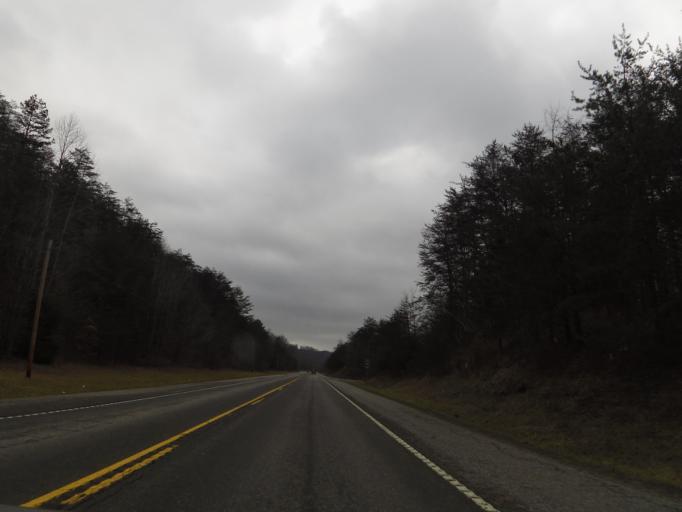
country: US
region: Tennessee
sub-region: Campbell County
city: Caryville
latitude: 36.4005
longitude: -84.2838
